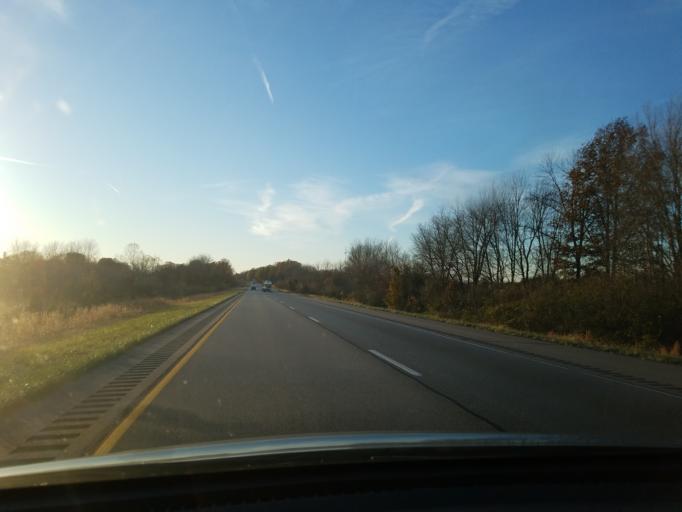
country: US
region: Indiana
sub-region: Warrick County
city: Chandler
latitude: 38.1844
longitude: -87.3793
